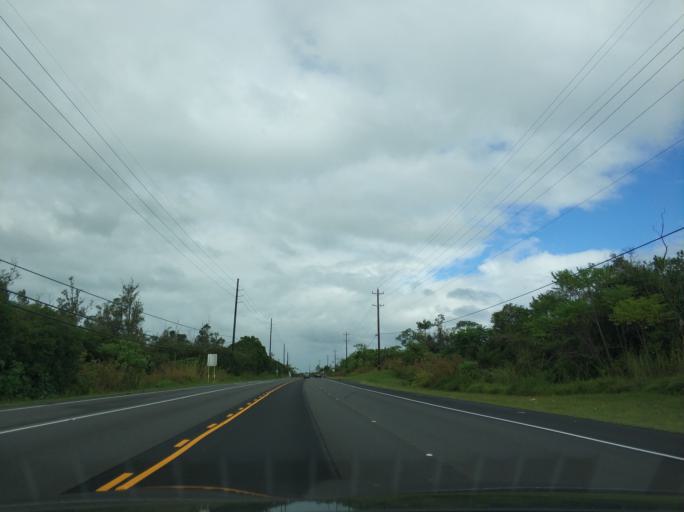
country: US
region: Hawaii
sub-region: Hawaii County
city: Orchidlands Estates
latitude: 19.5903
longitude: -155.0149
